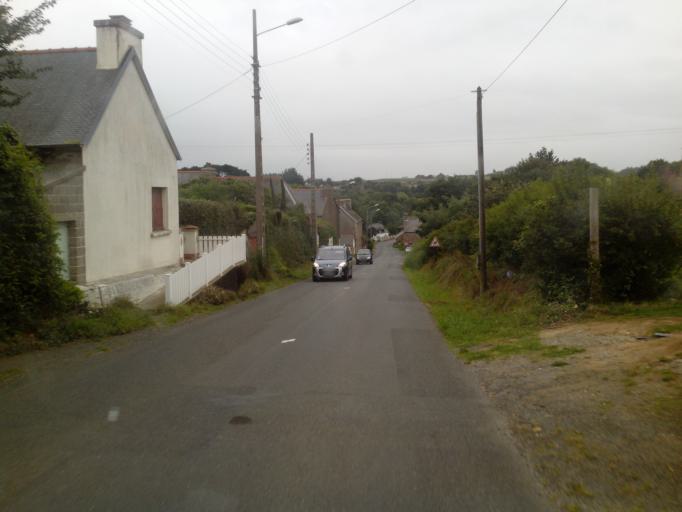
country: FR
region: Brittany
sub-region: Departement des Cotes-d'Armor
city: Pleubian
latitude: 48.8327
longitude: -3.1046
